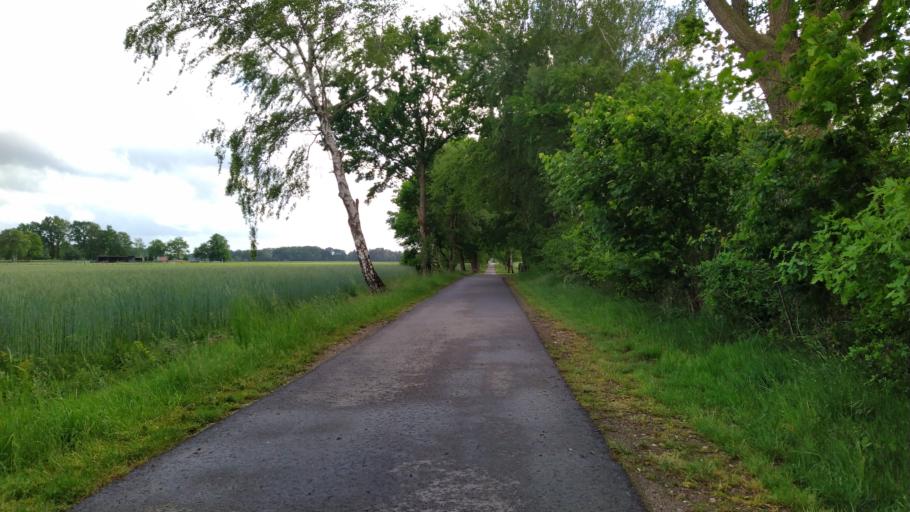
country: DE
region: Lower Saxony
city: Brest
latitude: 53.4420
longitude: 9.3641
